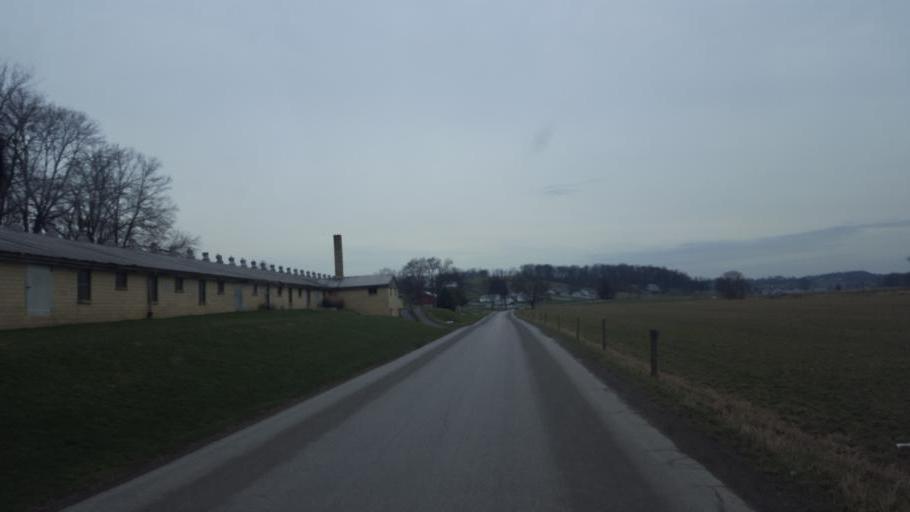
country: US
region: Ohio
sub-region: Tuscarawas County
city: Sugarcreek
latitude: 40.5169
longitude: -81.7370
